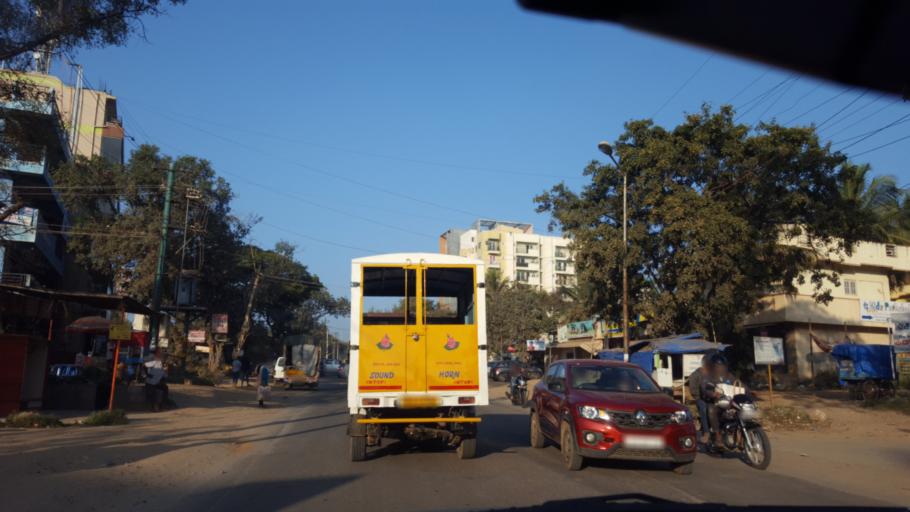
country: IN
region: Karnataka
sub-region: Bangalore Urban
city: Bangalore
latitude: 12.9284
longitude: 77.7392
